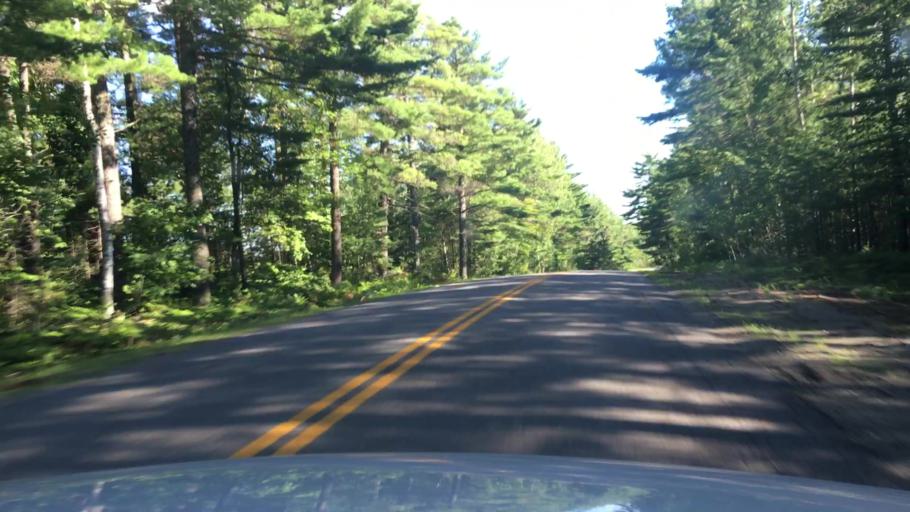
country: US
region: Maine
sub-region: Penobscot County
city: Enfield
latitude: 45.2296
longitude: -68.5803
